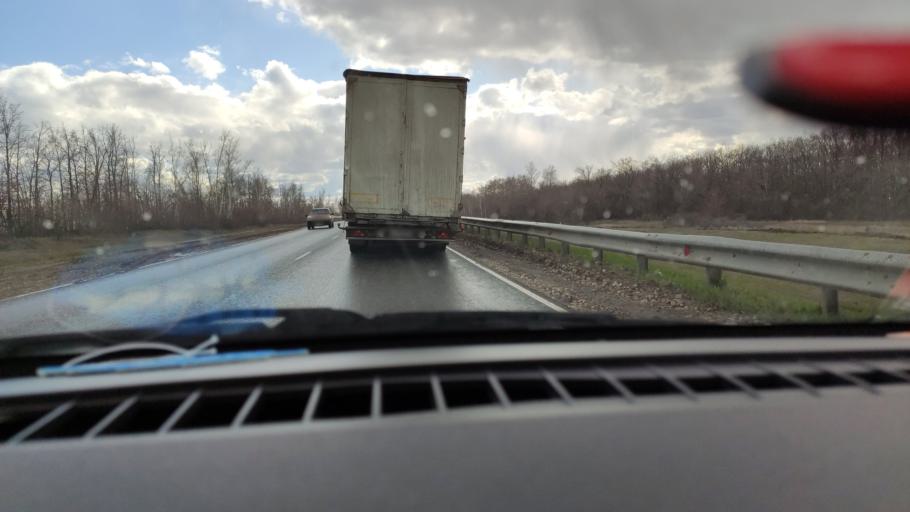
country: RU
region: Saratov
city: Balakovo
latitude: 52.0991
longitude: 47.7326
